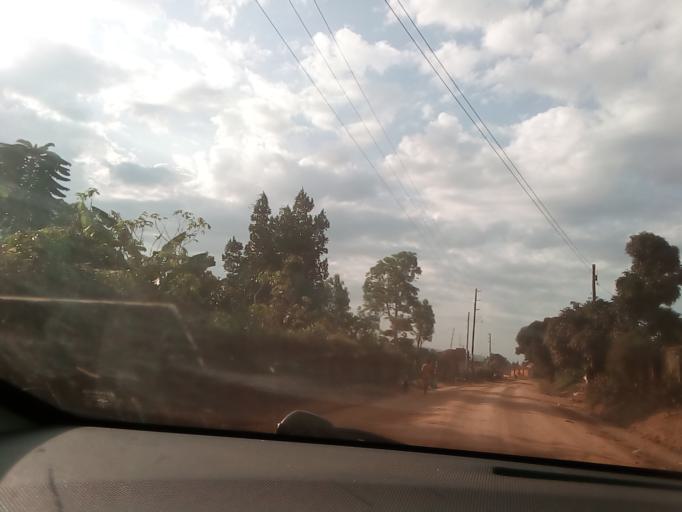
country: UG
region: Central Region
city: Masaka
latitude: -0.3494
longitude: 31.7171
